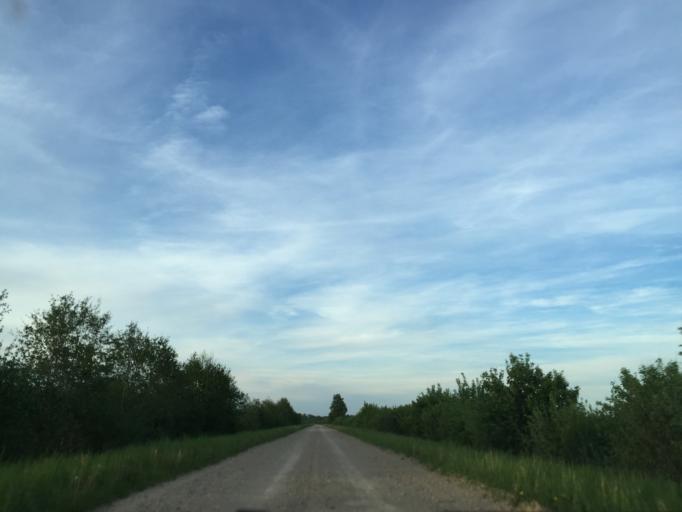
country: LV
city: Tireli
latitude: 56.7379
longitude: 23.5124
